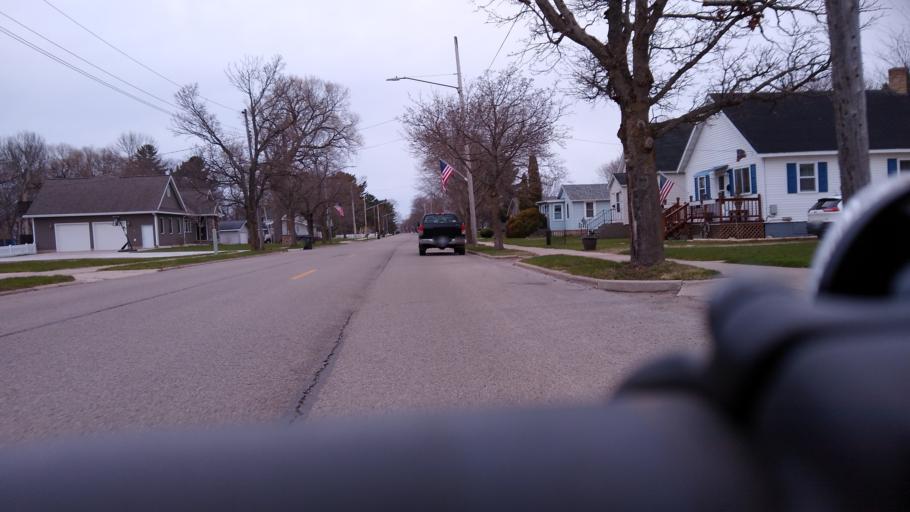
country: US
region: Michigan
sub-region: Delta County
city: Escanaba
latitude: 45.7304
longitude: -87.0642
